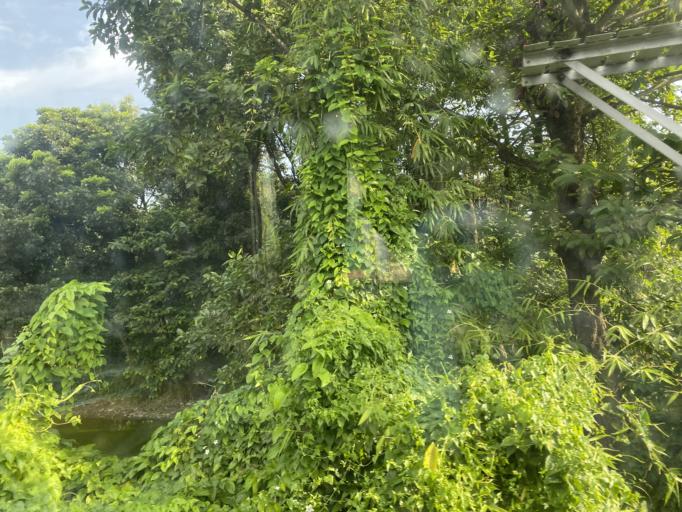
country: BD
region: Dhaka
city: Bhairab Bazar
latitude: 23.9671
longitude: 91.1157
